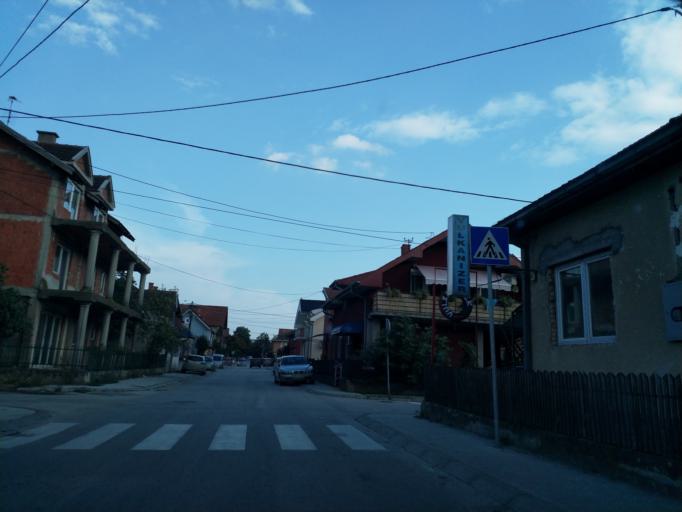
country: RS
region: Central Serbia
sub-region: Pomoravski Okrug
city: Jagodina
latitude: 43.9817
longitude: 21.2443
